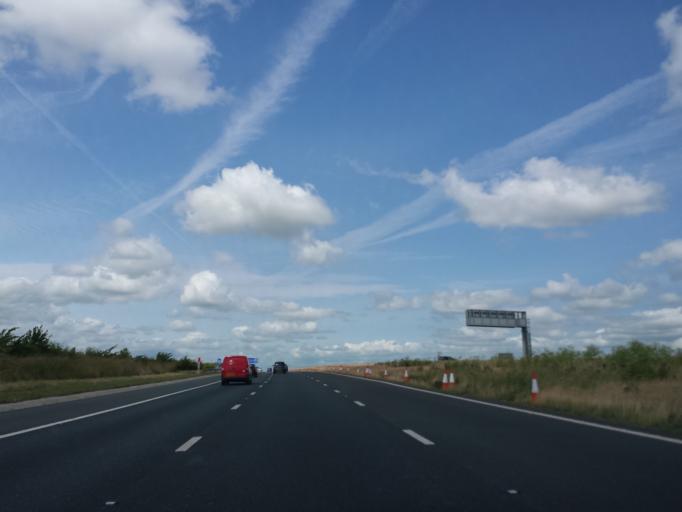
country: GB
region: England
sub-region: North Yorkshire
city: Ripon
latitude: 54.1715
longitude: -1.4522
